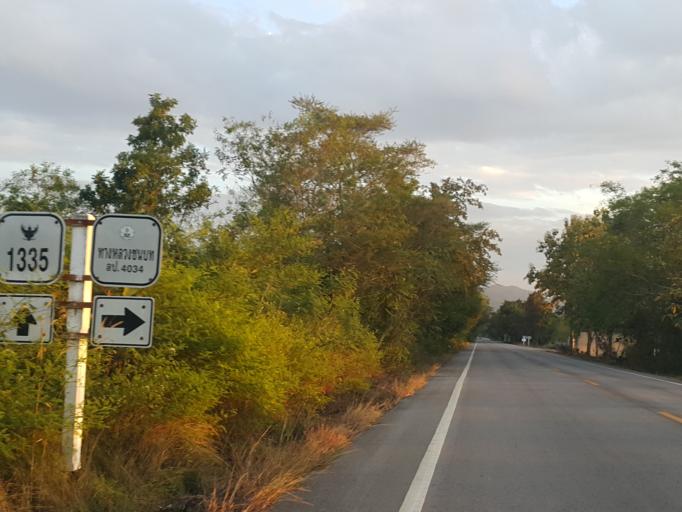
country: TH
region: Lampang
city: Mae Mo
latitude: 18.4352
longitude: 99.6411
